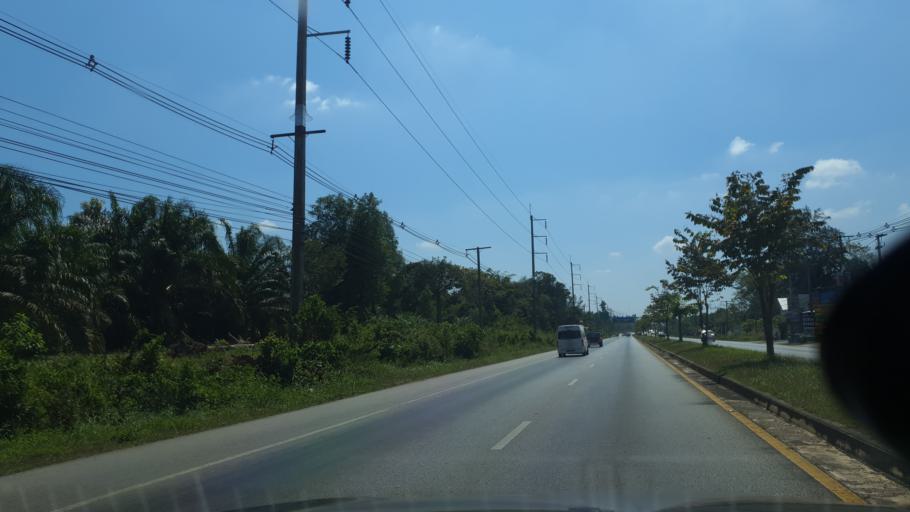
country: TH
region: Krabi
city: Khlong Thom
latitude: 7.9748
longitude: 99.1395
